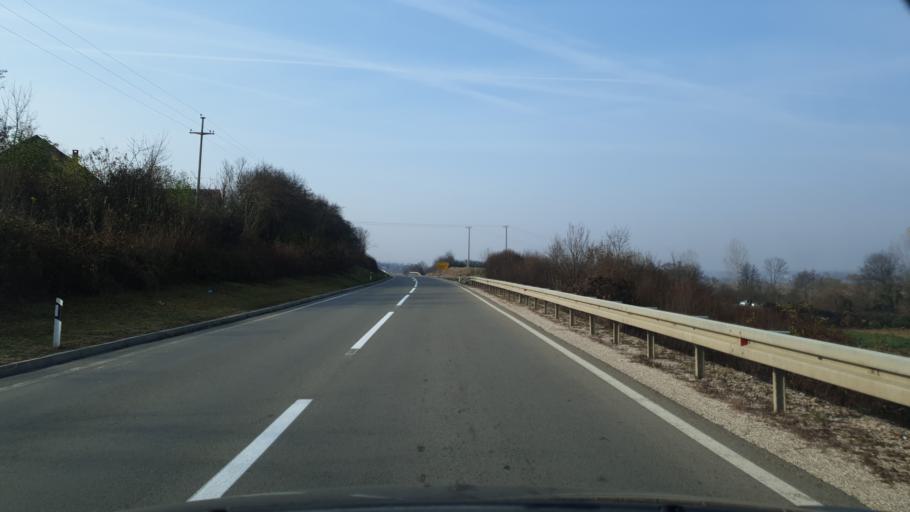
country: RS
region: Central Serbia
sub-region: Zajecarski Okrug
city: Boljevac
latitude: 43.9029
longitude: 22.0339
